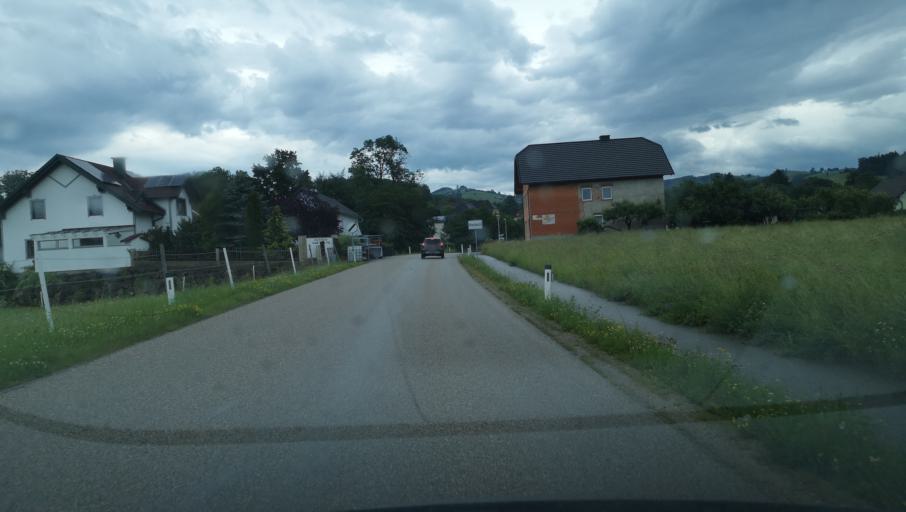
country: AT
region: Lower Austria
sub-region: Politischer Bezirk Amstetten
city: Neuhofen an der Ybbs
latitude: 48.0301
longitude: 14.8362
